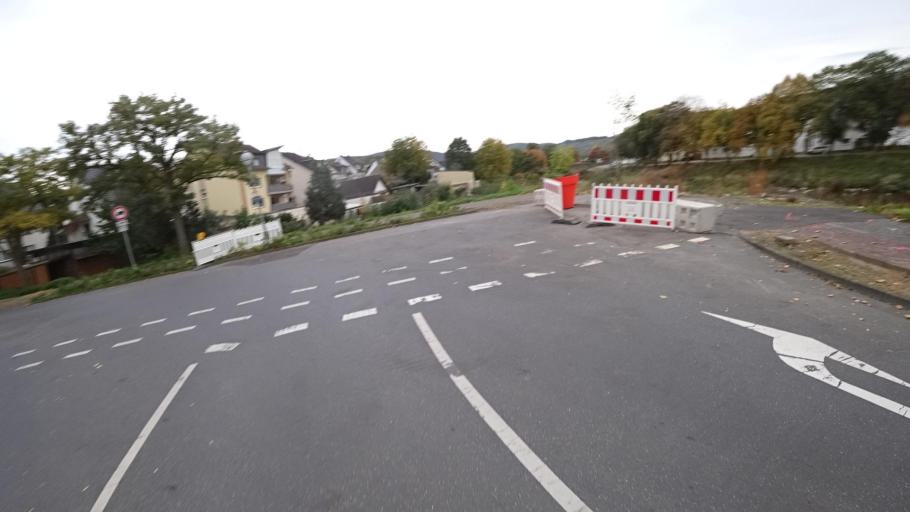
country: DE
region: Rheinland-Pfalz
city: Bad Neuenahr-Ahrweiler
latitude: 50.5392
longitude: 7.1072
